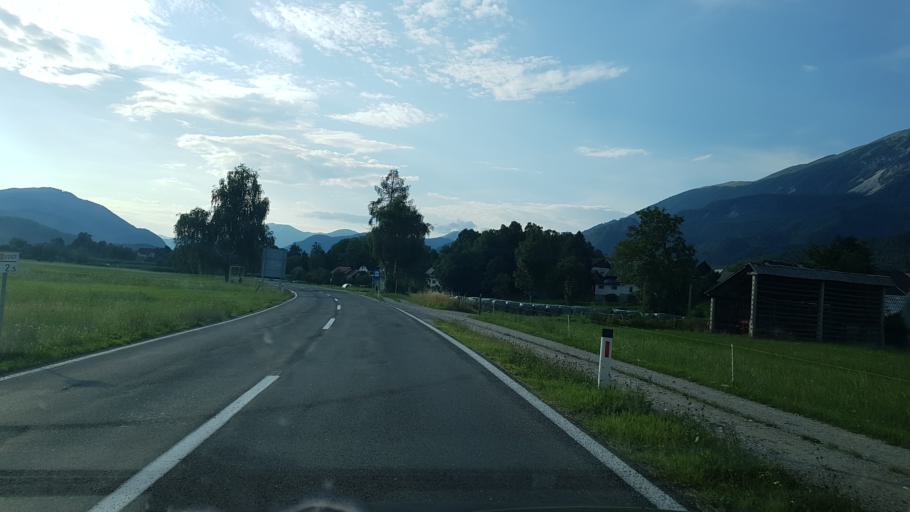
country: SI
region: Zirovnica
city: Zirovnica
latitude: 46.3869
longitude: 14.1463
